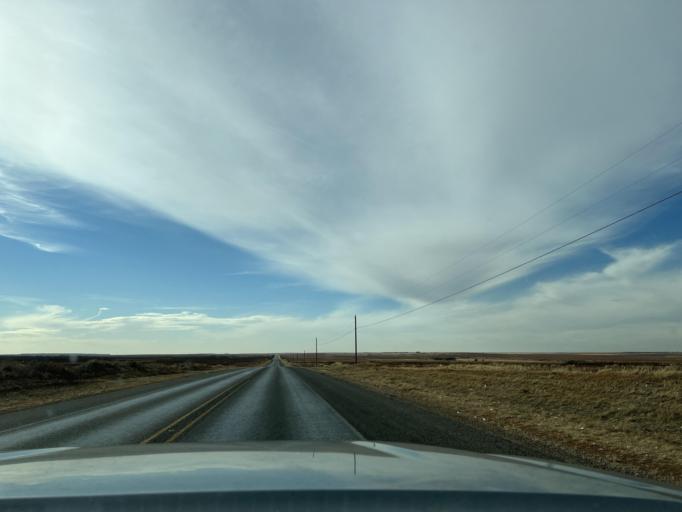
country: US
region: Texas
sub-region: Fisher County
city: Roby
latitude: 32.7415
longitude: -100.4582
